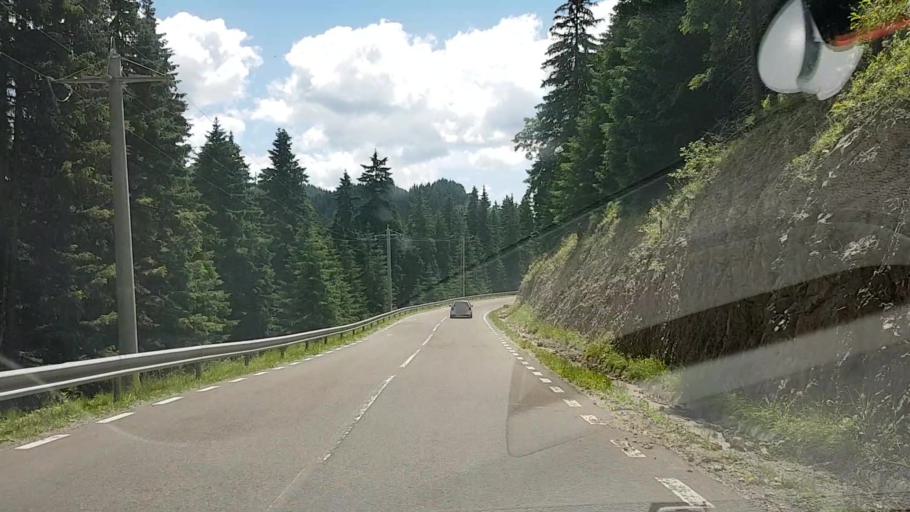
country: RO
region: Suceava
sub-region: Municipiul Campulung Moldovenesc
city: Campulung Moldovenesc
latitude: 47.4544
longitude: 25.5485
